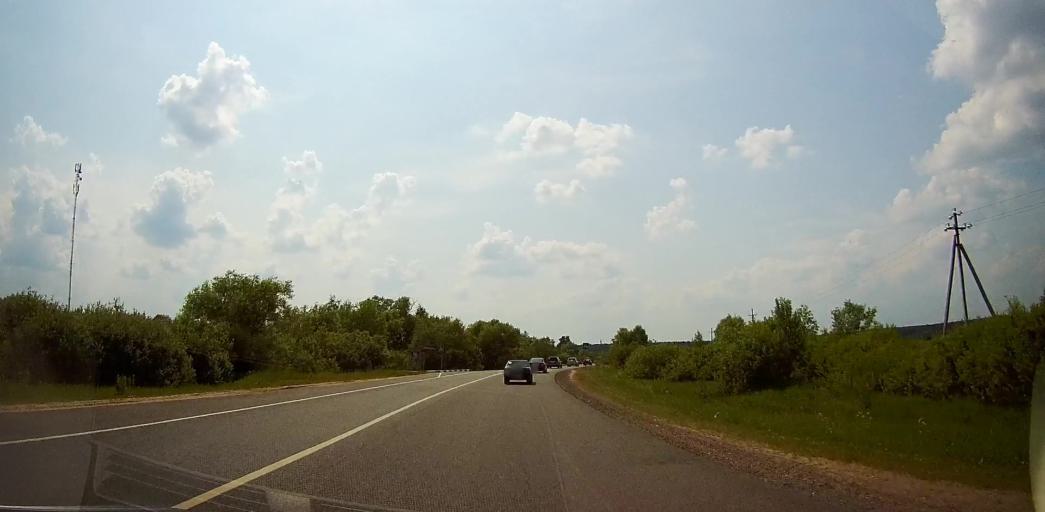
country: RU
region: Moskovskaya
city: Malino
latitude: 55.0622
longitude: 38.1539
